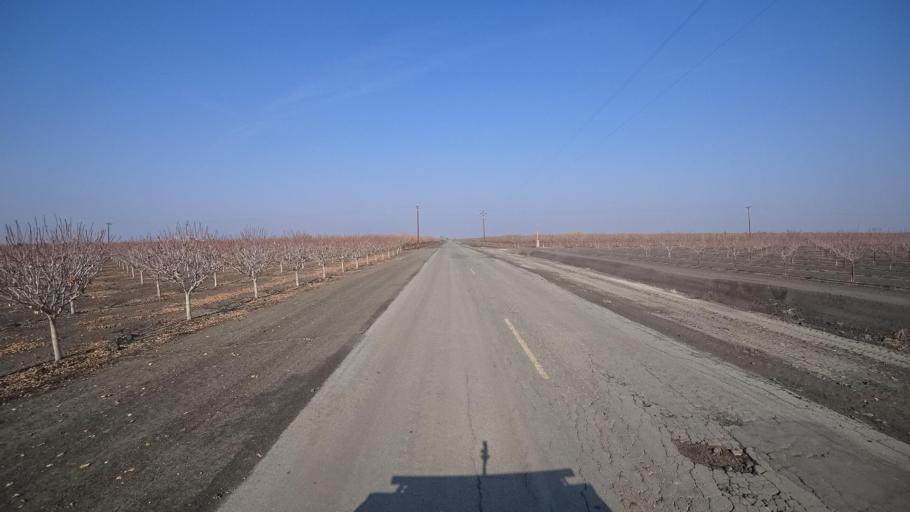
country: US
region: California
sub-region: Kern County
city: Buttonwillow
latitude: 35.3467
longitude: -119.4293
